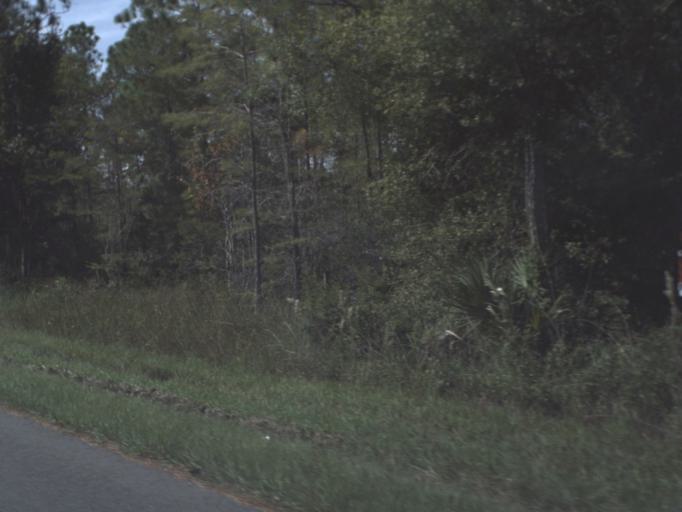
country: US
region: Florida
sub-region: Lee County
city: Olga
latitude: 26.9244
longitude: -81.7606
